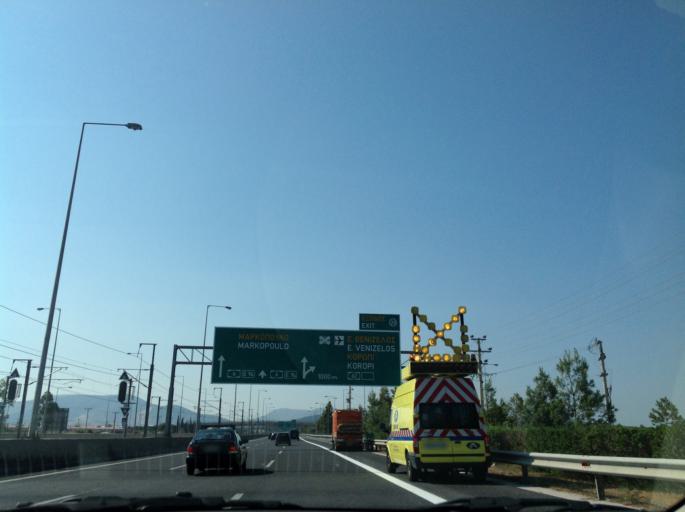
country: GR
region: Attica
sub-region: Nomarchia Anatolikis Attikis
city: Karellas
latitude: 37.9230
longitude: 23.8895
